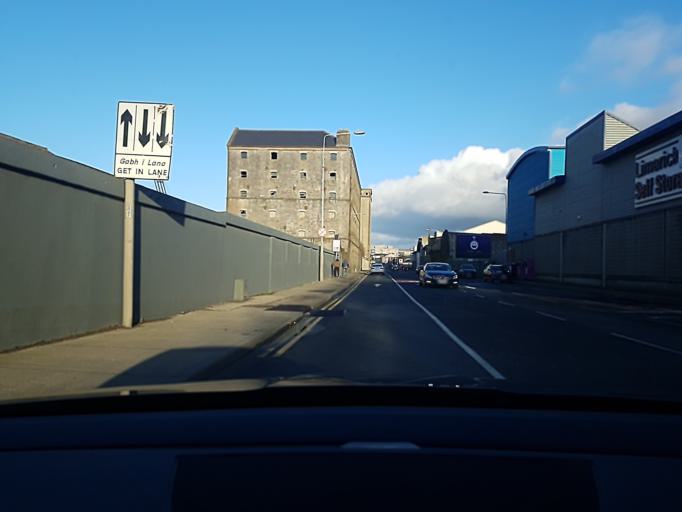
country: IE
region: Munster
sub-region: County Limerick
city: Luimneach
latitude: 52.6572
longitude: -8.6437
